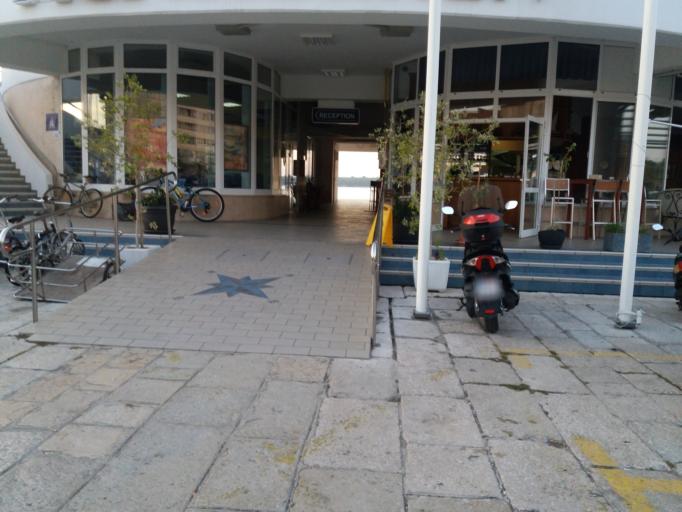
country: HR
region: Istarska
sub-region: Grad Pula
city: Pula
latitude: 44.8730
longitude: 13.8451
